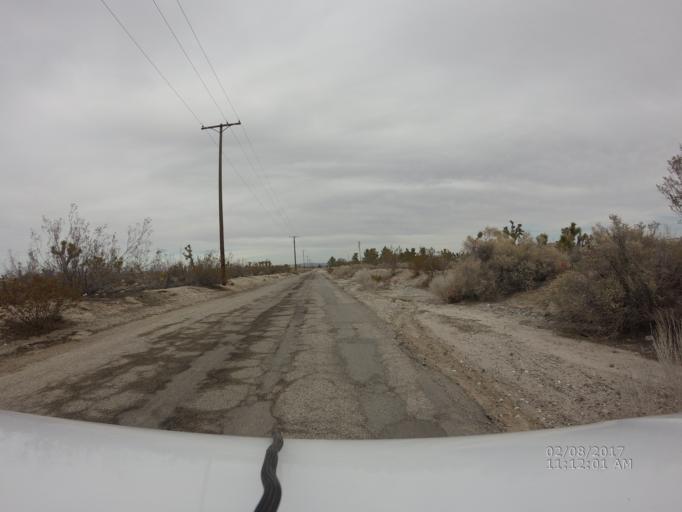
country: US
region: California
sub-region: San Bernardino County
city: Pinon Hills
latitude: 34.4830
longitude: -117.6600
